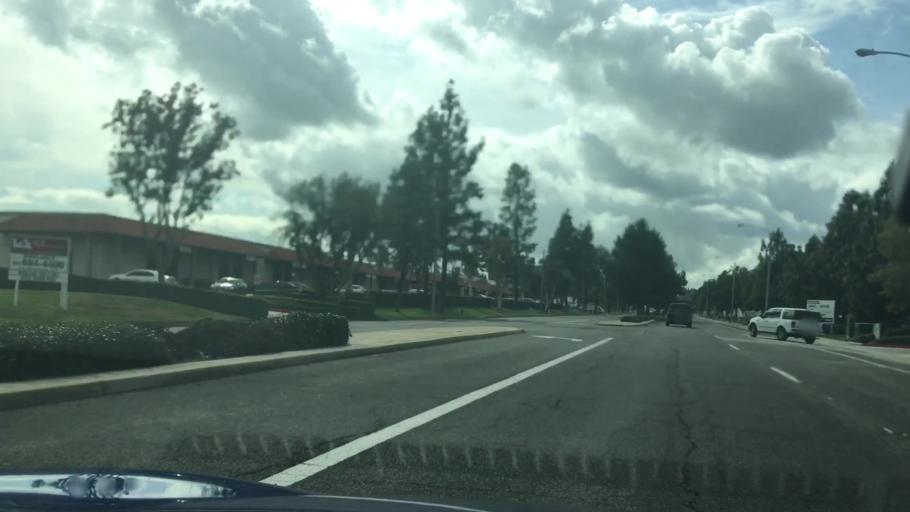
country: US
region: California
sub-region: Riverside County
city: Highgrove
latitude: 33.9943
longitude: -117.3485
